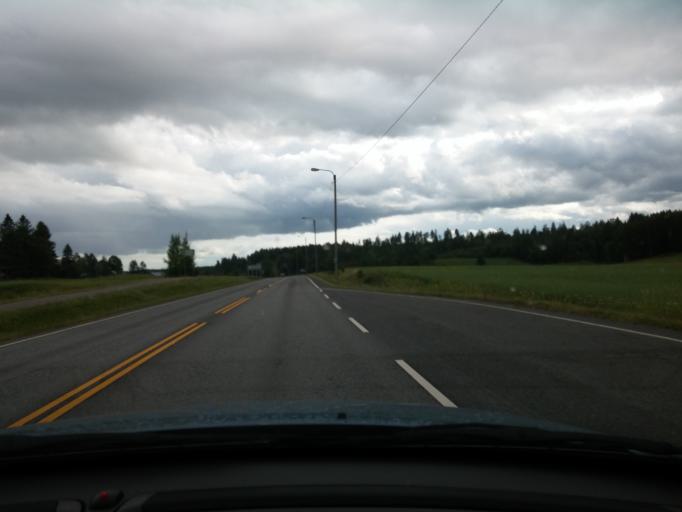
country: FI
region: Uusimaa
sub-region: Porvoo
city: Askola
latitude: 60.5239
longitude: 25.5806
